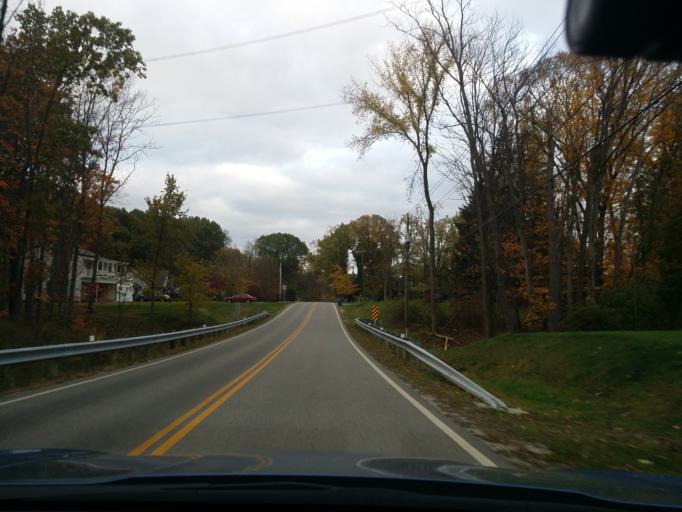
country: US
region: Ohio
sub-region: Cuyahoga County
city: Berea
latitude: 41.3884
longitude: -81.8775
